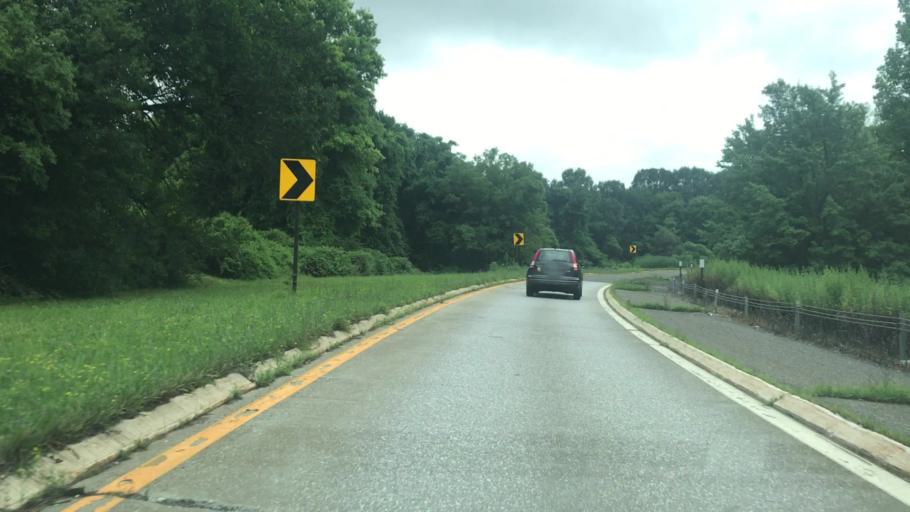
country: US
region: New York
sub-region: Westchester County
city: Hawthorne
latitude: 41.1116
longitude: -73.8039
